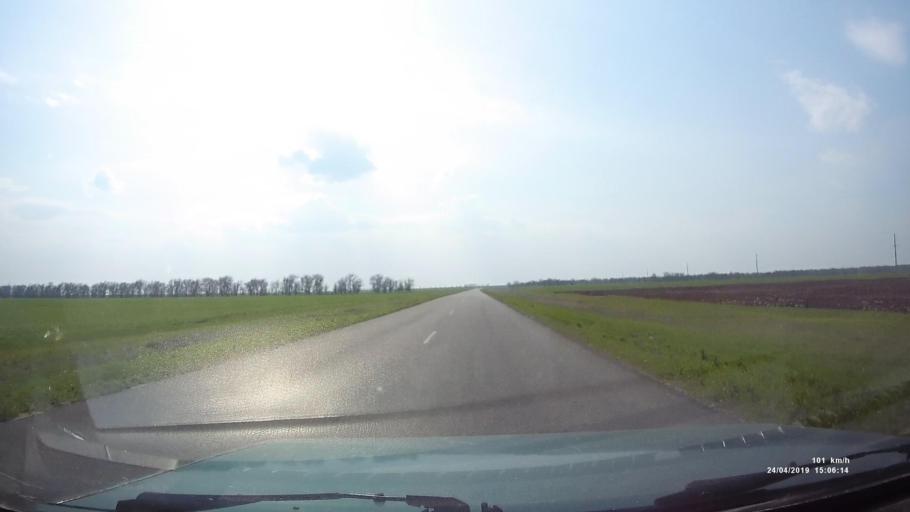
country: RU
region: Rostov
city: Remontnoye
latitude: 46.5589
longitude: 43.4323
